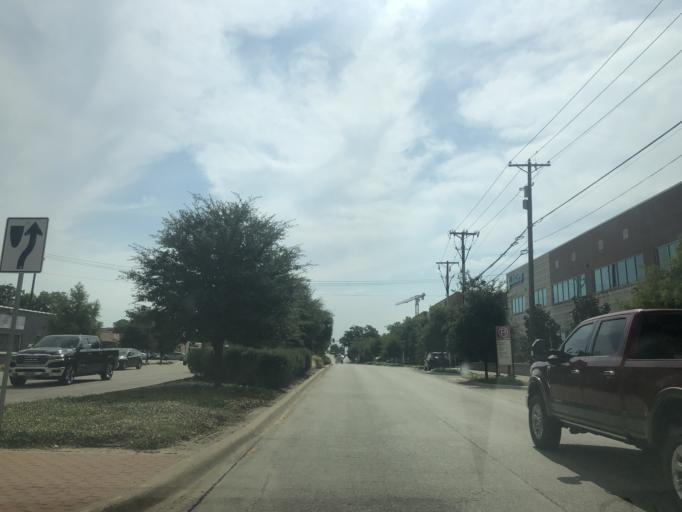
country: US
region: Texas
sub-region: Tarrant County
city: Fort Worth
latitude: 32.7330
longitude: -97.3349
